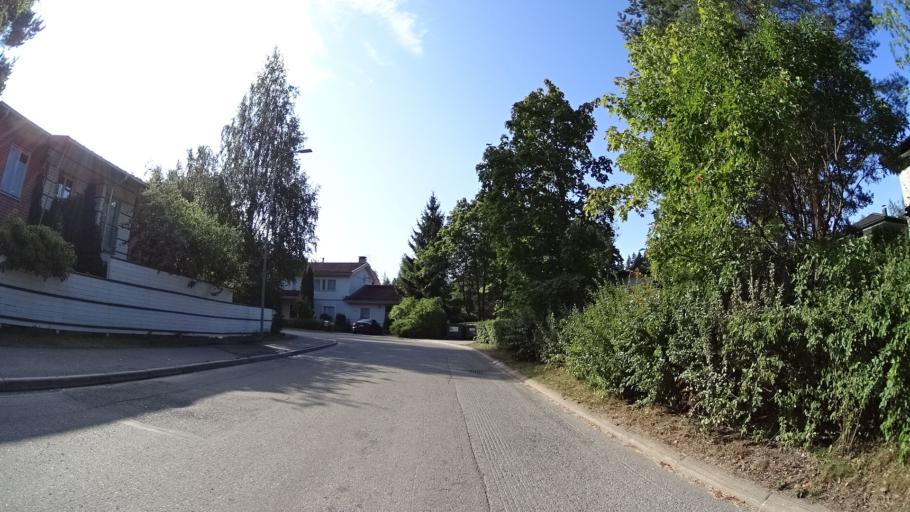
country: FI
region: Uusimaa
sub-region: Helsinki
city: Kilo
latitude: 60.1995
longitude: 24.7987
